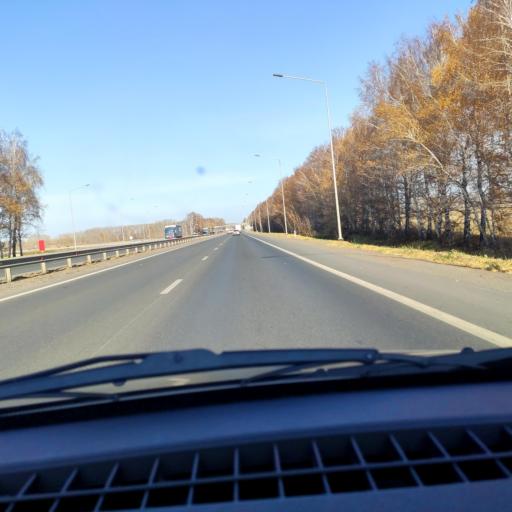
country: RU
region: Bashkortostan
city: Ufa
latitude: 54.5418
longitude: 55.9142
